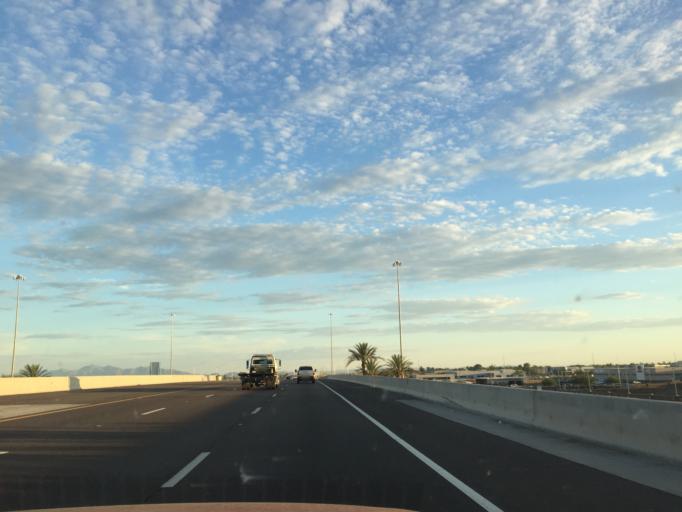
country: US
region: Arizona
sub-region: Maricopa County
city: Citrus Park
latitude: 33.6107
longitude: -112.4184
